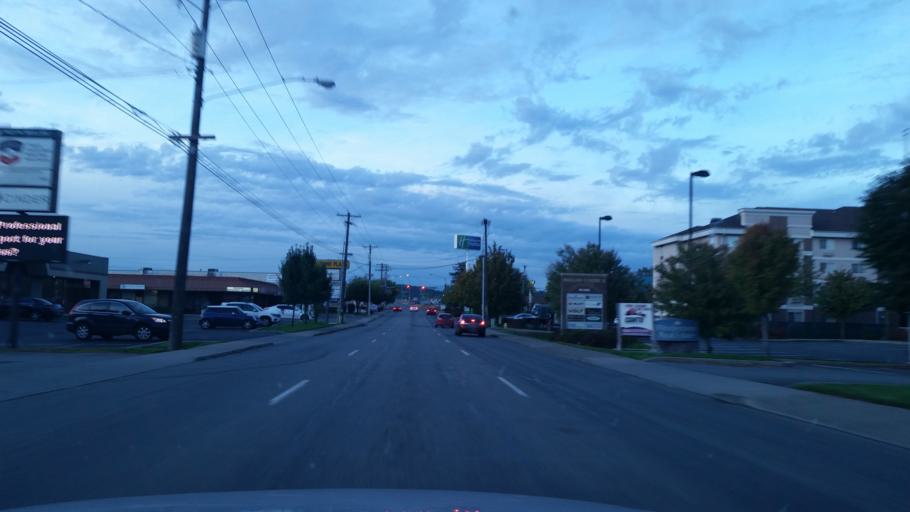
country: US
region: Washington
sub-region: Spokane County
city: Dishman
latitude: 47.6698
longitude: -117.2816
